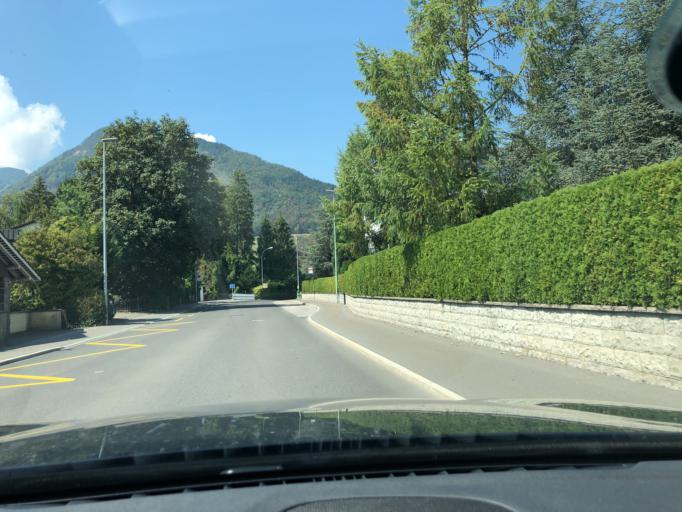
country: CH
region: Schwyz
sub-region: Bezirk Schwyz
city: Ibach
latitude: 47.0231
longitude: 8.6405
